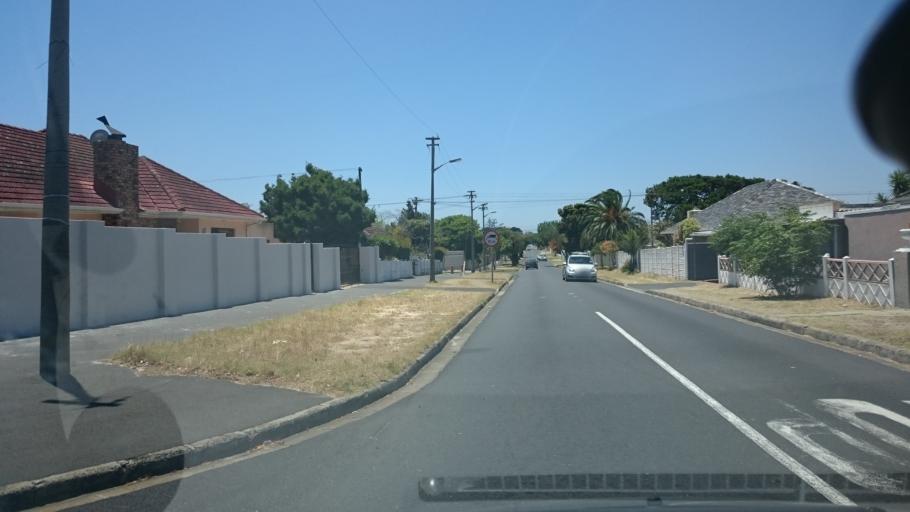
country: ZA
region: Western Cape
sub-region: City of Cape Town
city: Retreat
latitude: -34.0252
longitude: 18.4777
